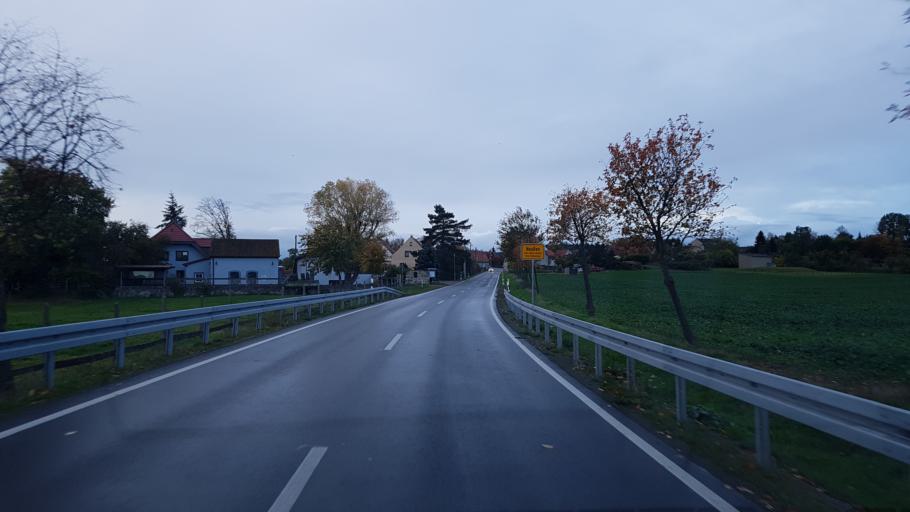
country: DE
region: Saxony
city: Belgern
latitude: 51.4542
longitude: 13.1156
